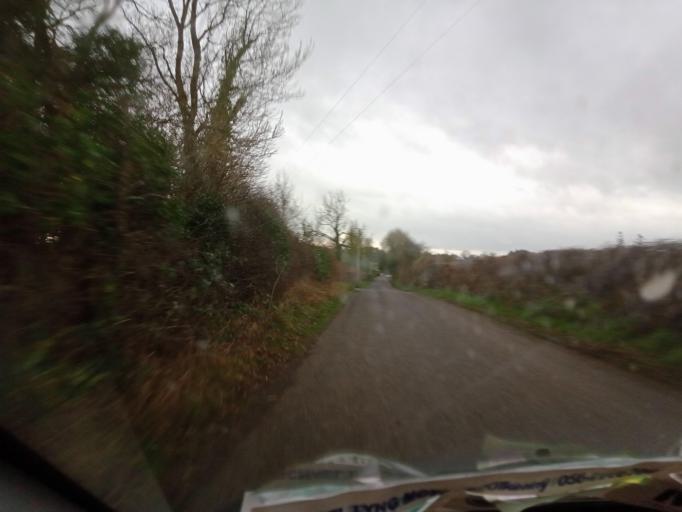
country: IE
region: Munster
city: Fethard
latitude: 52.5379
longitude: -7.7597
